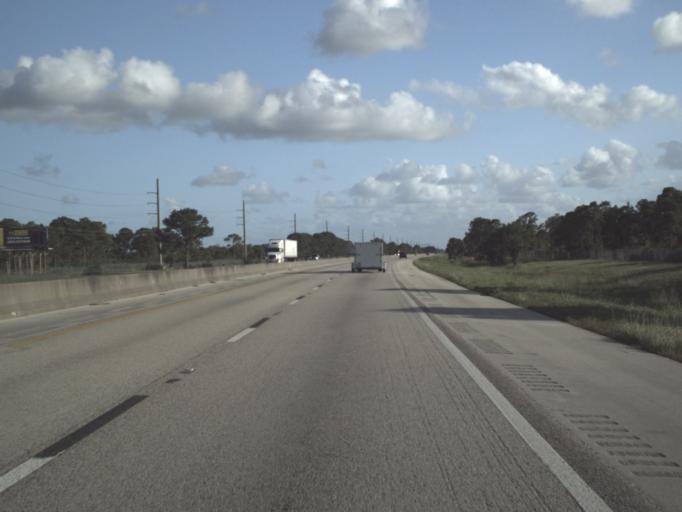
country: US
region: Florida
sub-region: Saint Lucie County
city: Port Saint Lucie
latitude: 27.2572
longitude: -80.3498
